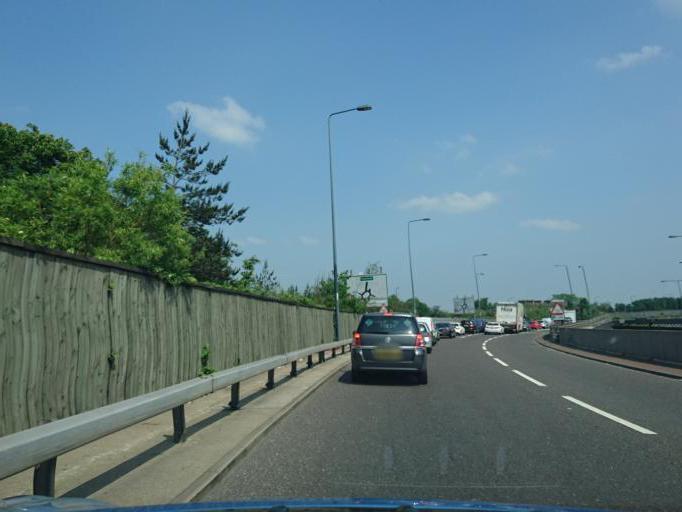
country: GB
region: England
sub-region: Greater London
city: Woodford Green
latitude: 51.5728
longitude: 0.0137
